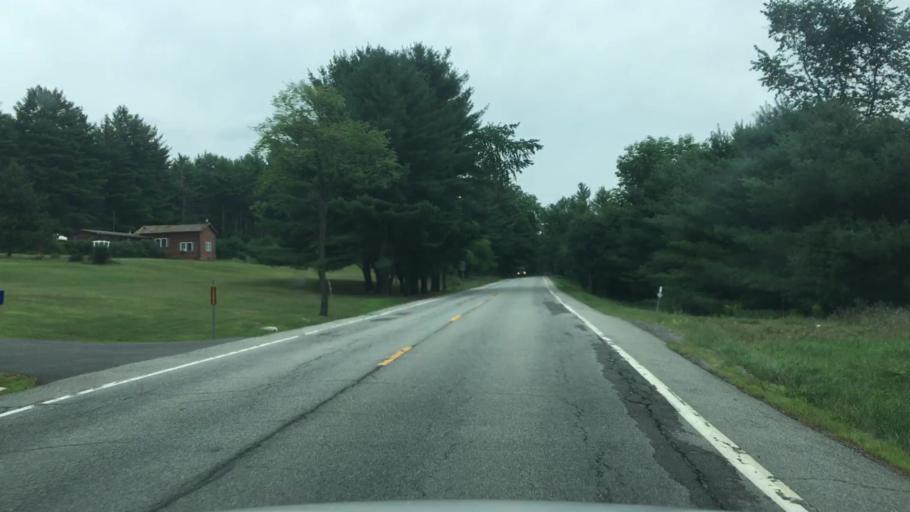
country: US
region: New York
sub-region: Essex County
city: Elizabethtown
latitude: 44.3924
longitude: -73.7098
